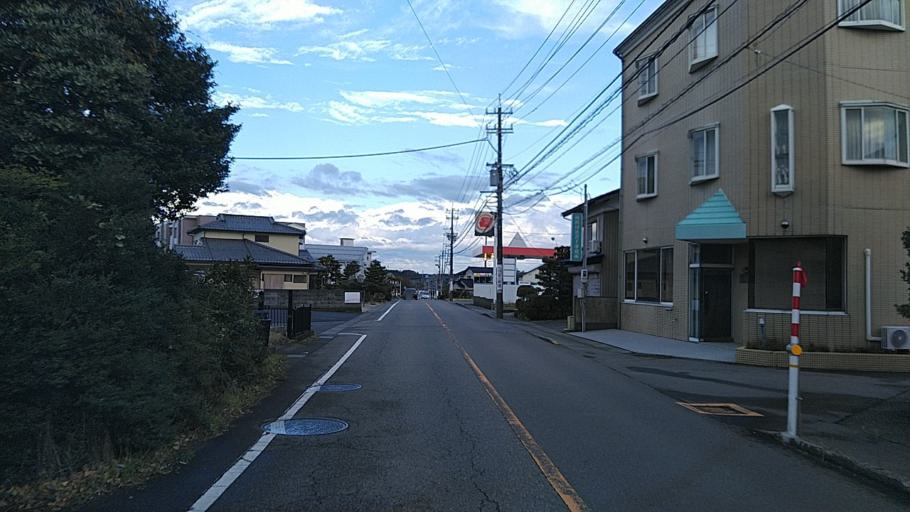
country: JP
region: Ishikawa
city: Komatsu
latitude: 36.2913
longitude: 136.3559
